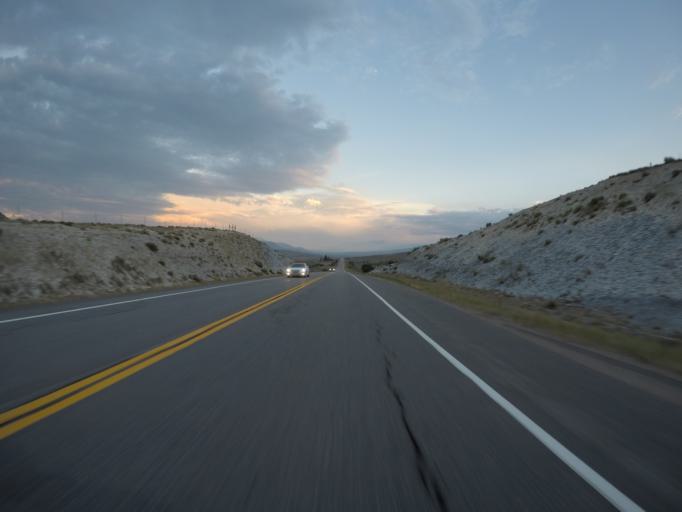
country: US
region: Colorado
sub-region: Grand County
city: Kremmling
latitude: 40.1100
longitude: -106.4265
